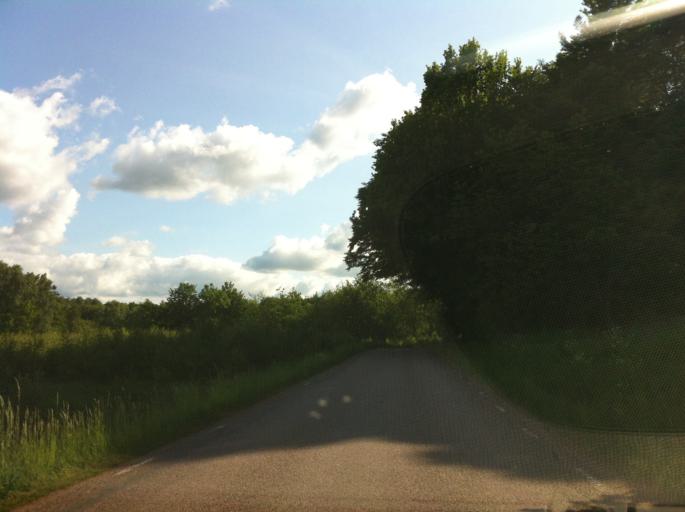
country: SE
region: Skane
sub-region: Klippans Kommun
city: Ljungbyhed
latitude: 56.0578
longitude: 13.2160
